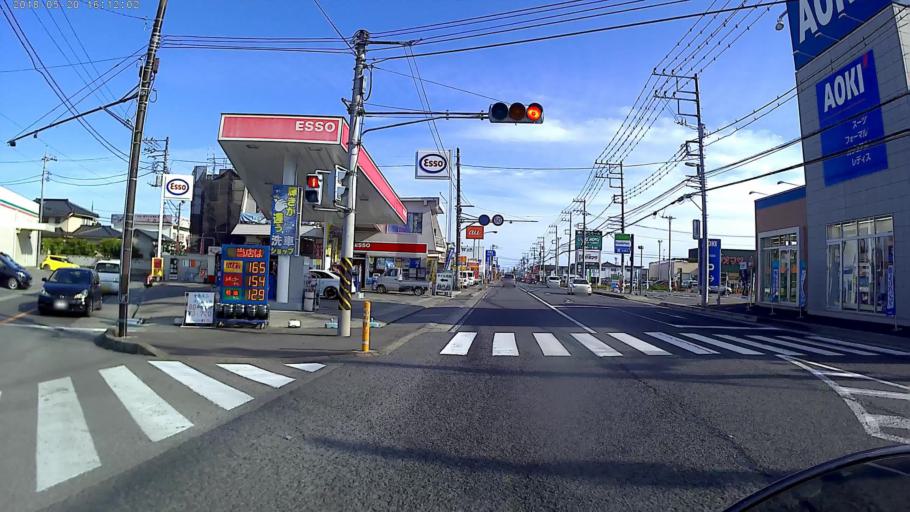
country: JP
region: Kanagawa
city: Odawara
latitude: 35.3240
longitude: 139.1586
